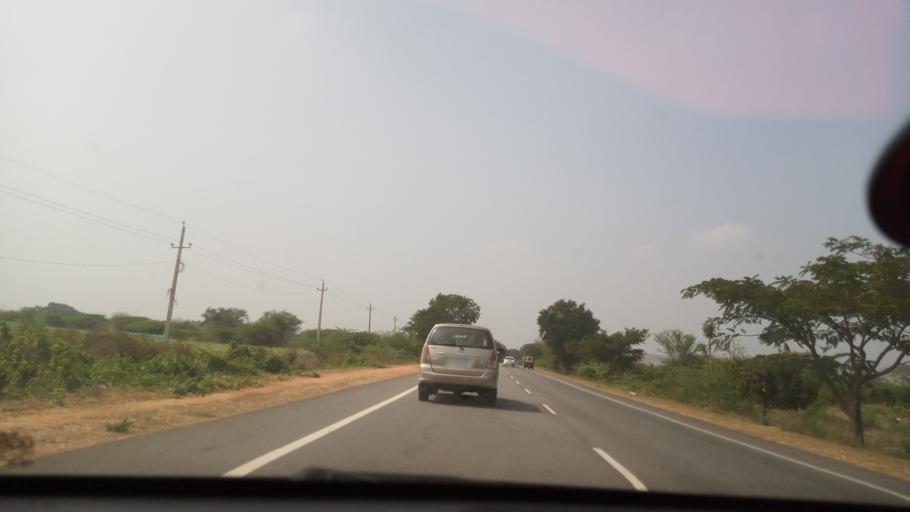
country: IN
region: Karnataka
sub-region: Mysore
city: Nanjangud
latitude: 12.0740
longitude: 76.7415
